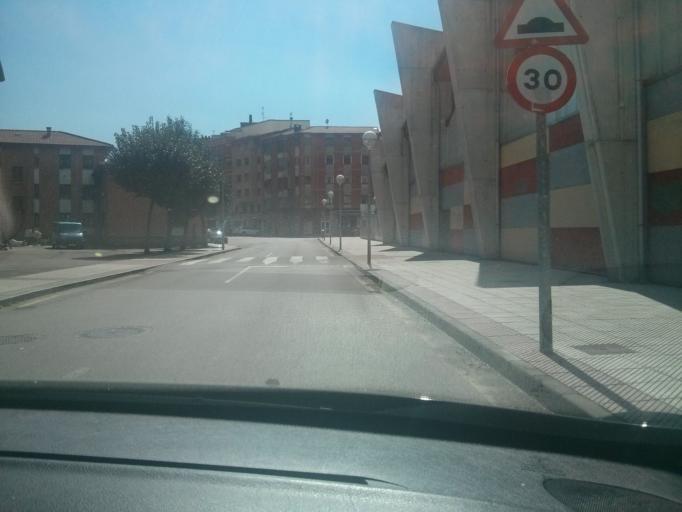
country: ES
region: Asturias
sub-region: Province of Asturias
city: Mieres
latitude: 43.2565
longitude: -5.7794
